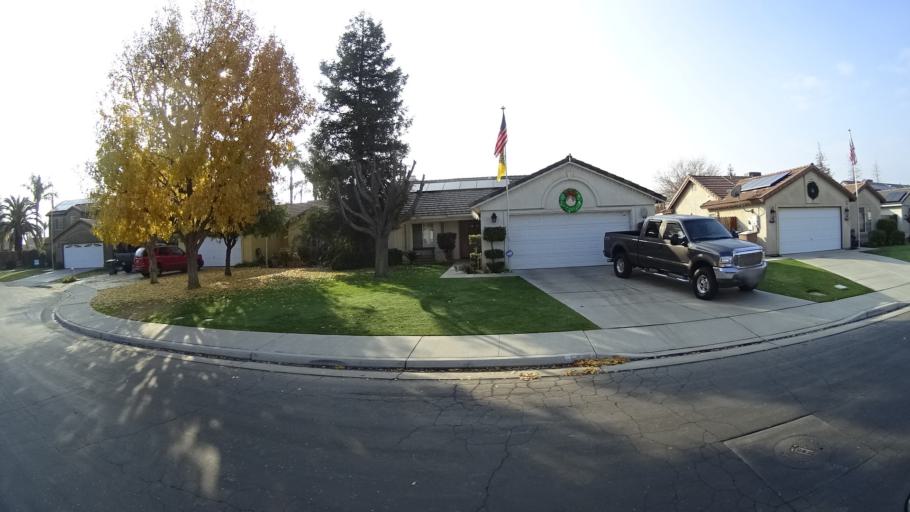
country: US
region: California
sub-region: Kern County
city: Greenfield
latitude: 35.3053
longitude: -119.0640
